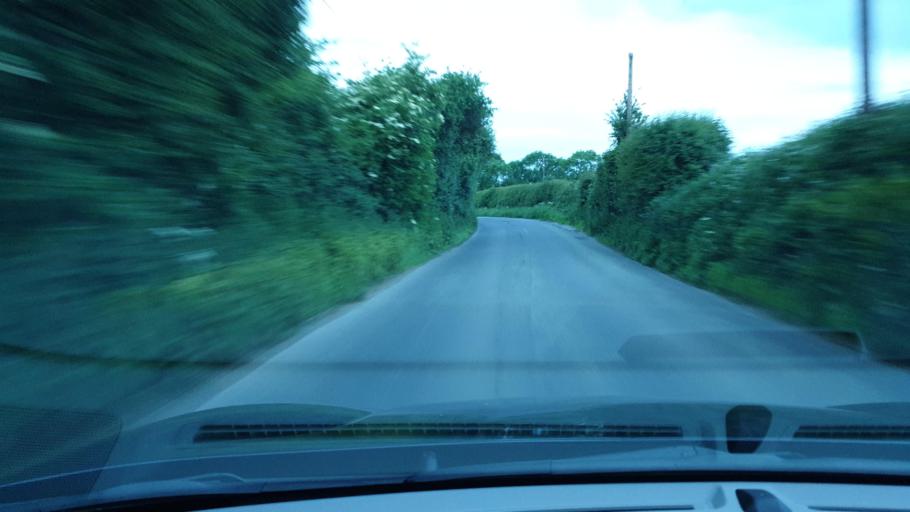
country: IE
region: Leinster
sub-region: An Mhi
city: Ashbourne
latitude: 53.5698
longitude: -6.3916
